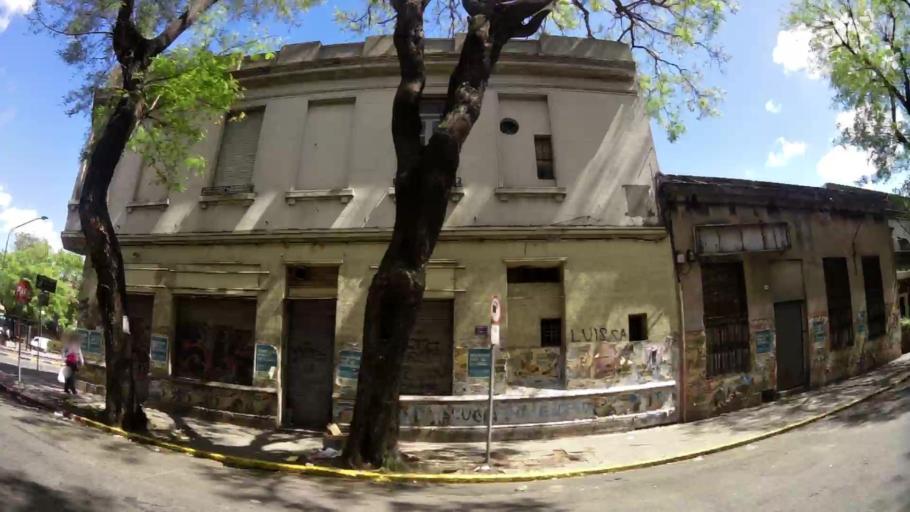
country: UY
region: Montevideo
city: Montevideo
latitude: -34.8848
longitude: -56.1931
